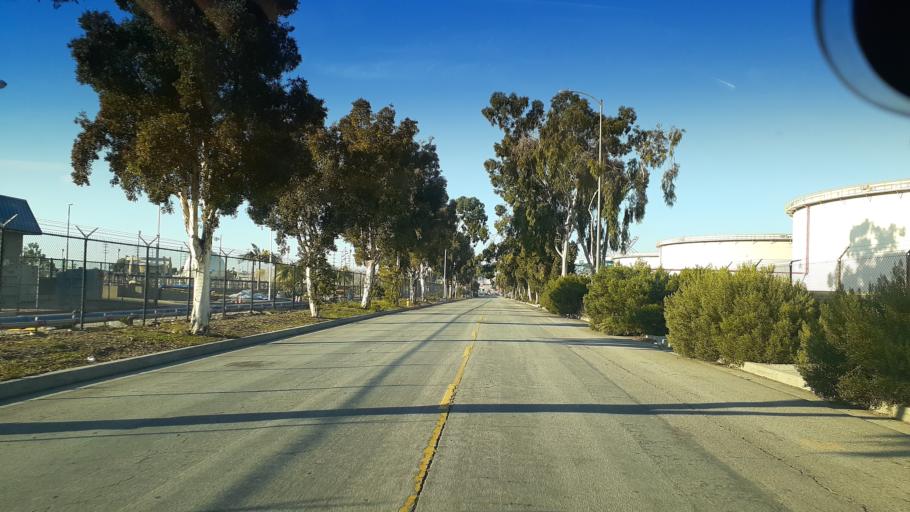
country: US
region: California
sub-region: Los Angeles County
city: San Pedro
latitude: 33.7453
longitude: -118.2622
